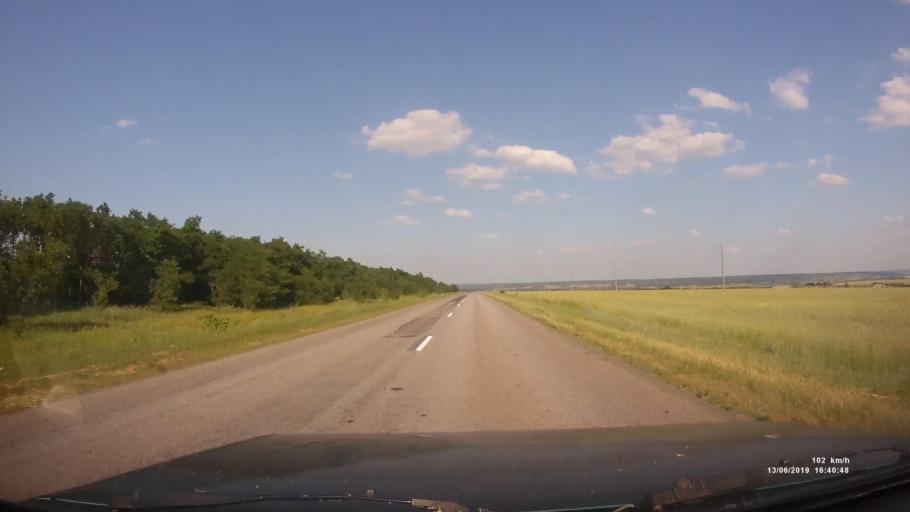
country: RU
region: Rostov
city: Kazanskaya
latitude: 49.9328
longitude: 41.3693
